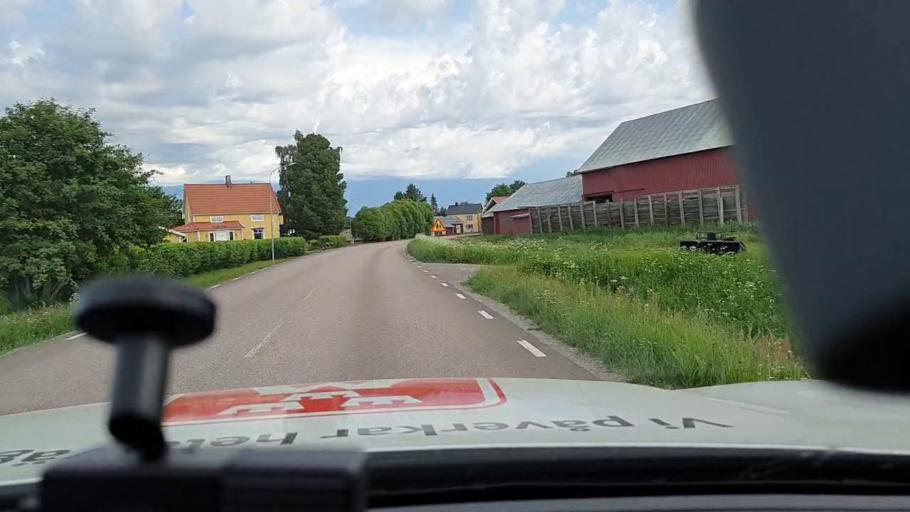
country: SE
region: Norrbotten
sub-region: Bodens Kommun
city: Saevast
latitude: 65.7083
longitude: 21.7610
